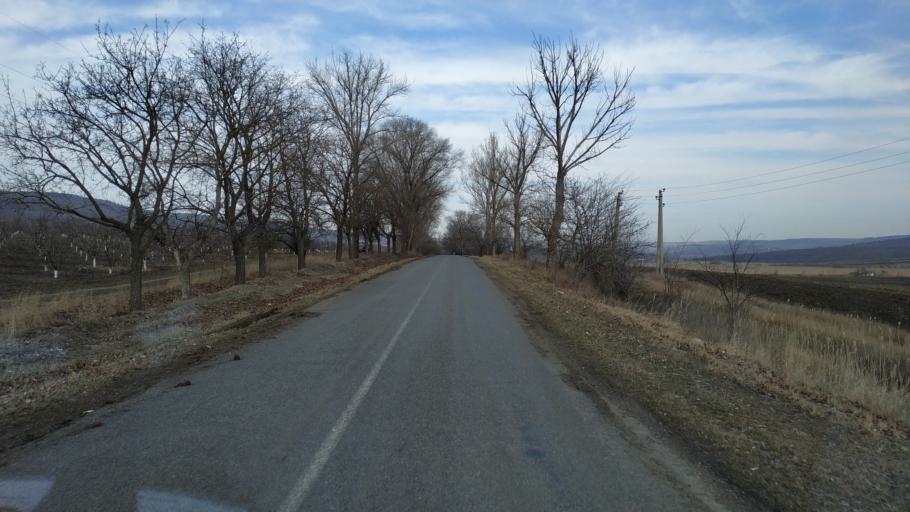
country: MD
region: Nisporeni
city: Nisporeni
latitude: 47.0987
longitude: 28.1304
